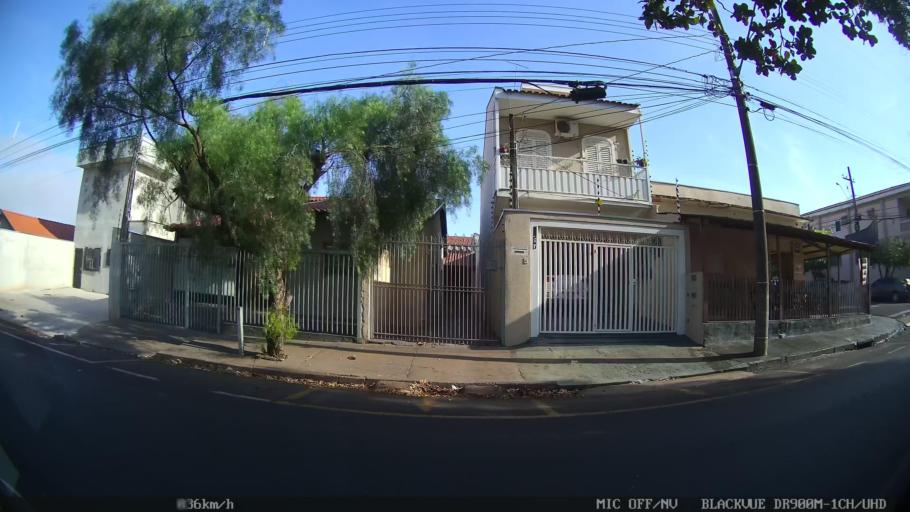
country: BR
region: Sao Paulo
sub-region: Sao Jose Do Rio Preto
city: Sao Jose do Rio Preto
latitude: -20.7871
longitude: -49.4107
